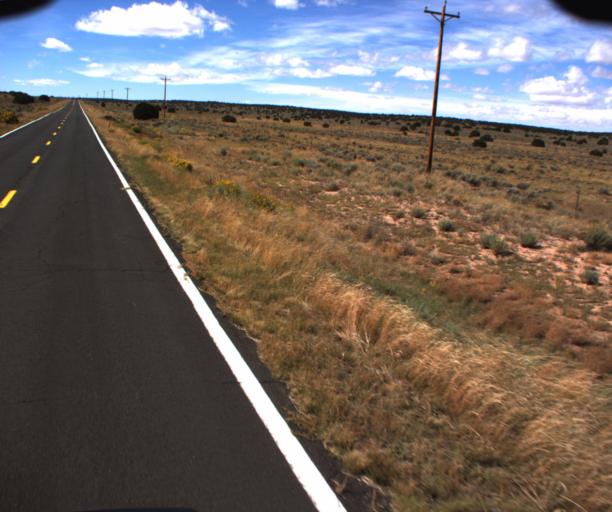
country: US
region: New Mexico
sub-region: McKinley County
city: Zuni Pueblo
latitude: 35.0082
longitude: -109.0743
